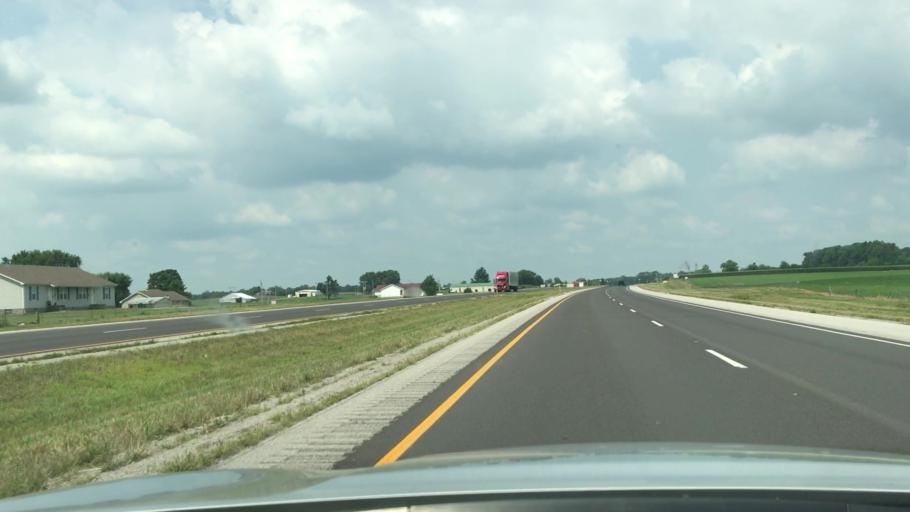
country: US
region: Kentucky
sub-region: Todd County
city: Elkton
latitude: 36.8029
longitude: -87.0890
